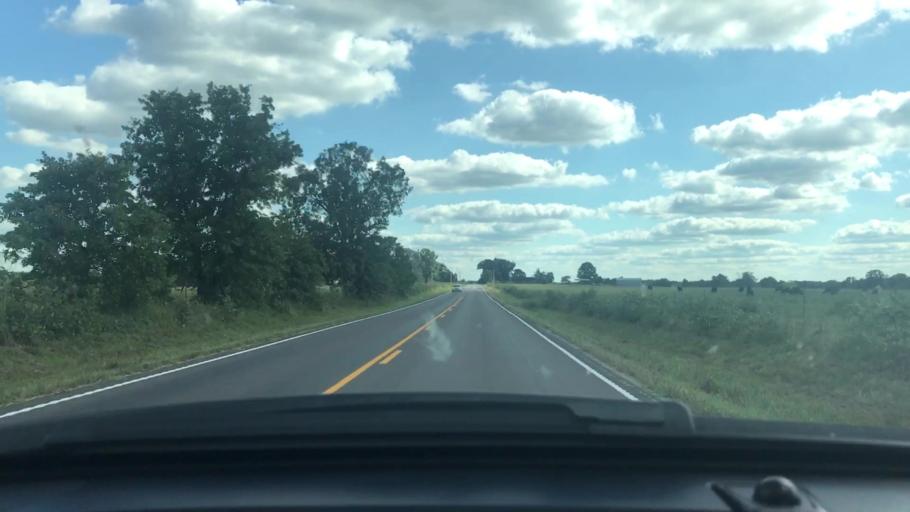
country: US
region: Missouri
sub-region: Wright County
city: Mountain Grove
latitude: 37.2679
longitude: -92.3081
